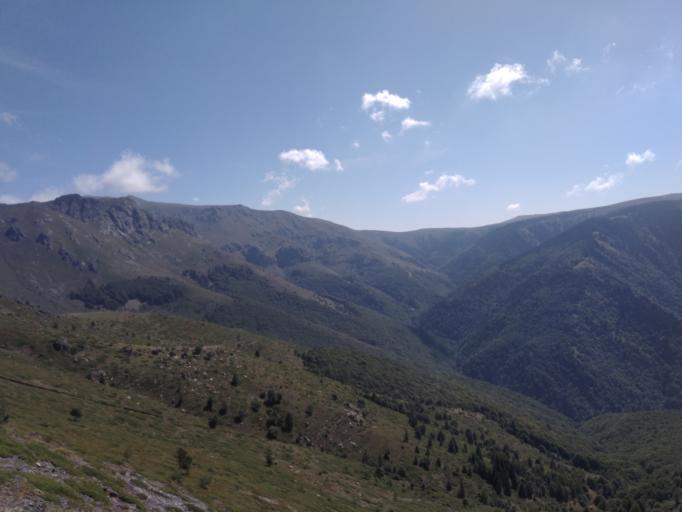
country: BG
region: Plovdiv
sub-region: Obshtina Karlovo
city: Karlovo
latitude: 42.7147
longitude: 24.8168
